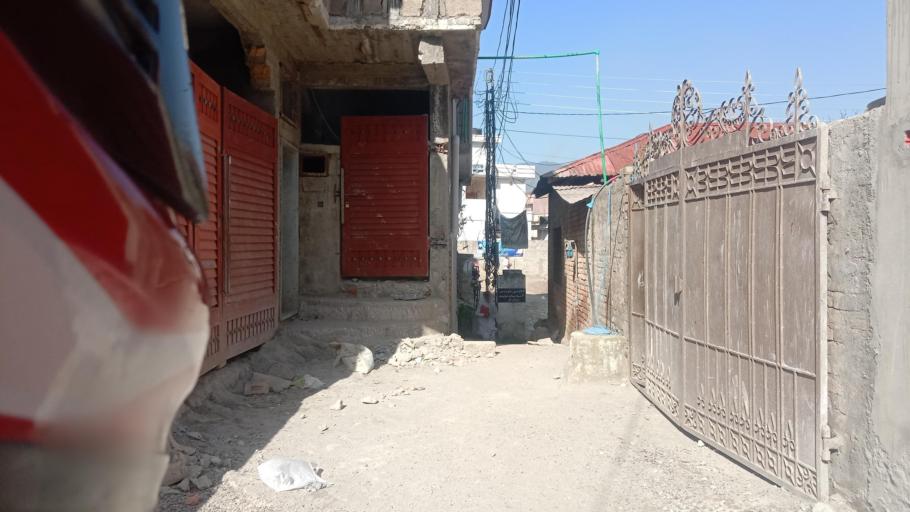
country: PK
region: Khyber Pakhtunkhwa
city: Abbottabad
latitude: 34.1796
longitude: 73.2242
